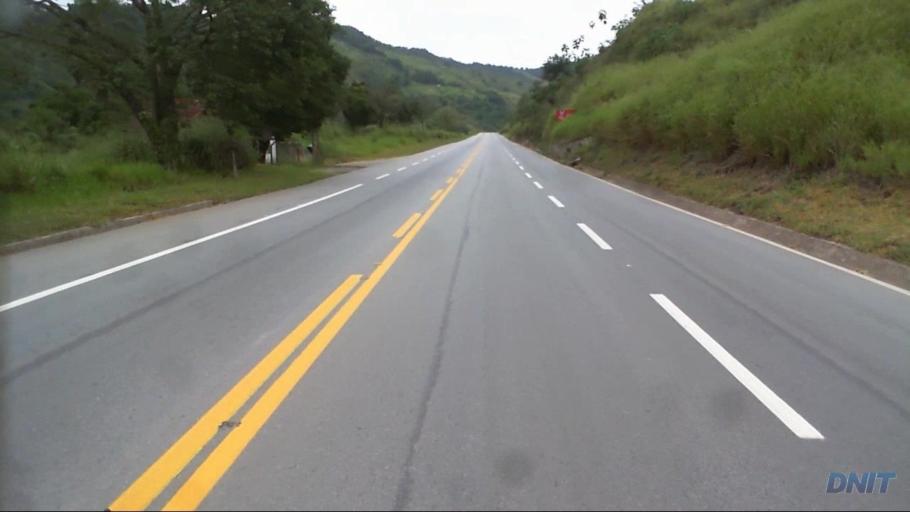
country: BR
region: Minas Gerais
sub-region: Timoteo
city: Timoteo
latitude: -19.6323
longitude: -42.8072
